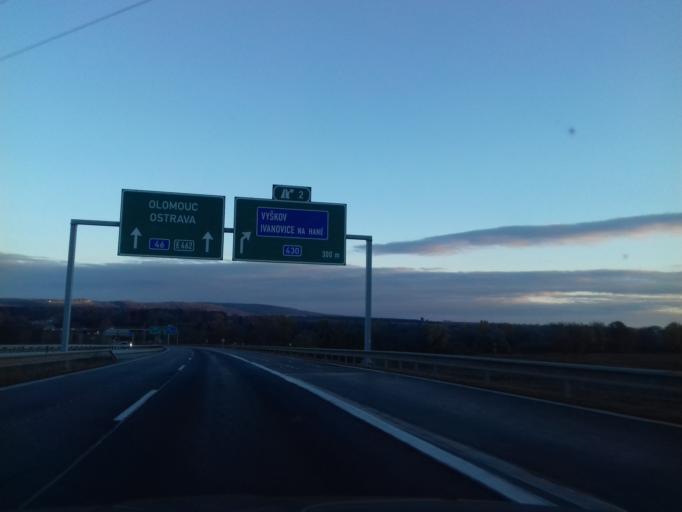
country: CZ
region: South Moravian
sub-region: Okres Vyskov
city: Vyskov
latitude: 49.2747
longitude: 17.0211
